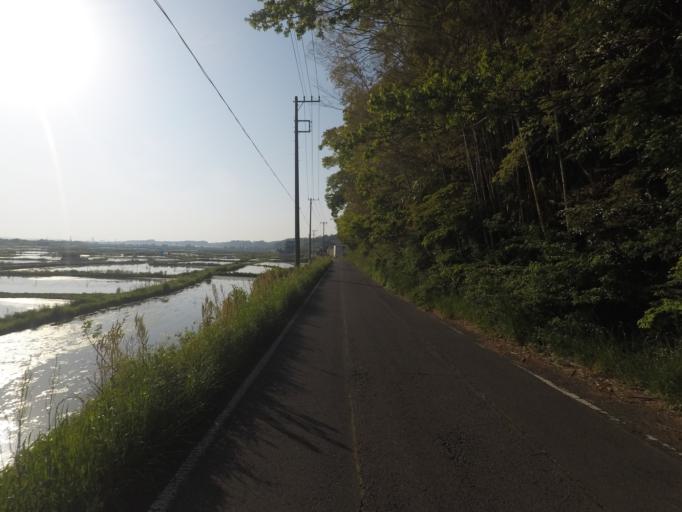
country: JP
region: Ibaraki
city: Ami
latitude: 36.0653
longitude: 140.2874
